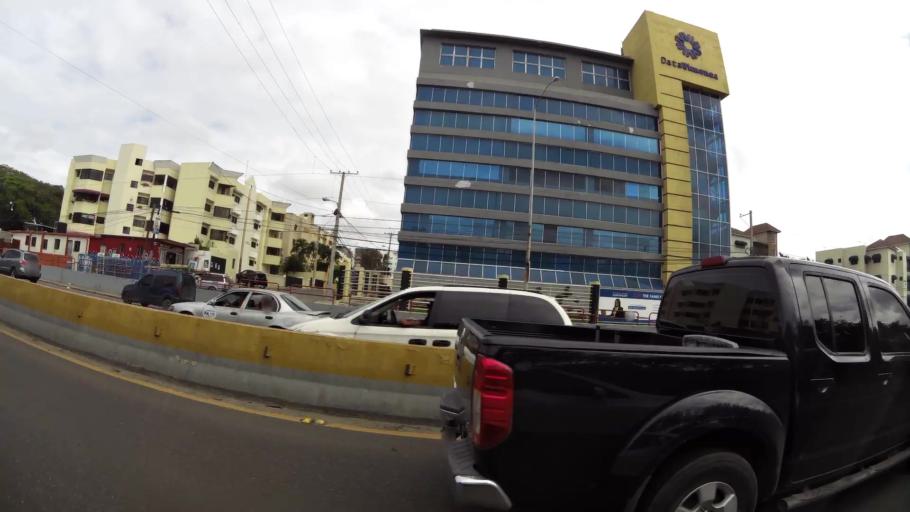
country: DO
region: Santiago
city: Santiago de los Caballeros
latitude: 19.4489
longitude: -70.6817
